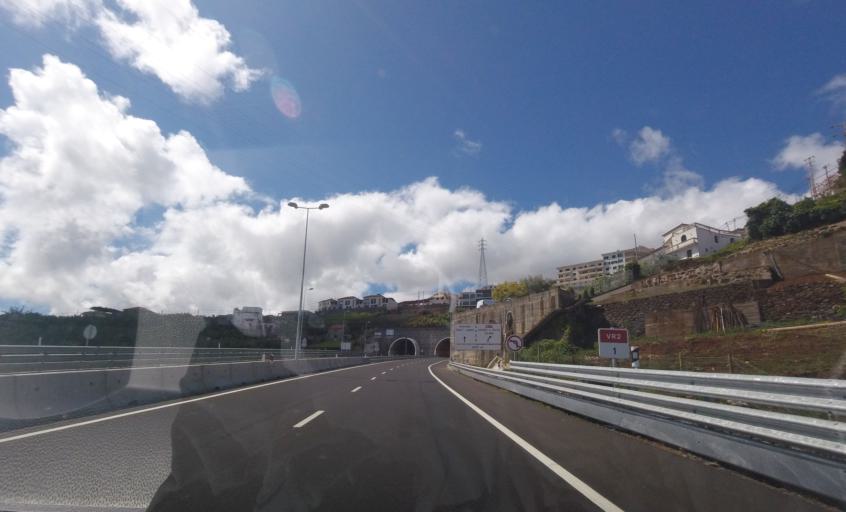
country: PT
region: Madeira
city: Camara de Lobos
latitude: 32.6627
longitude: -16.9682
